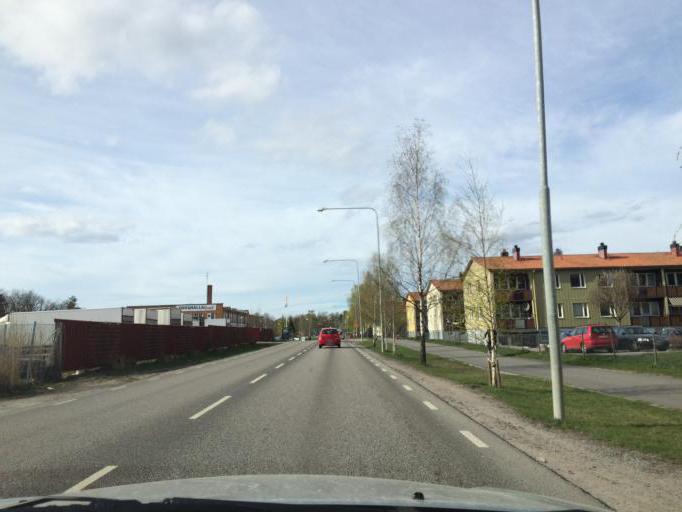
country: SE
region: Soedermanland
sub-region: Eskilstuna Kommun
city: Torshalla
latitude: 59.4138
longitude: 16.4753
